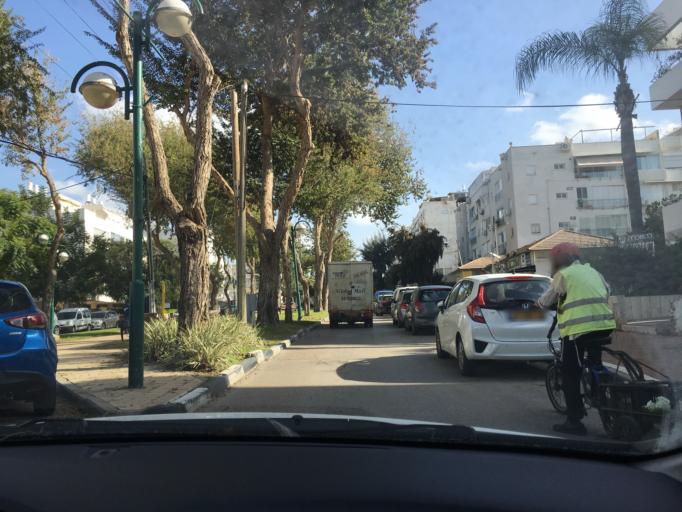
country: IL
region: Tel Aviv
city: Ramat HaSharon
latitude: 32.1465
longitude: 34.8366
